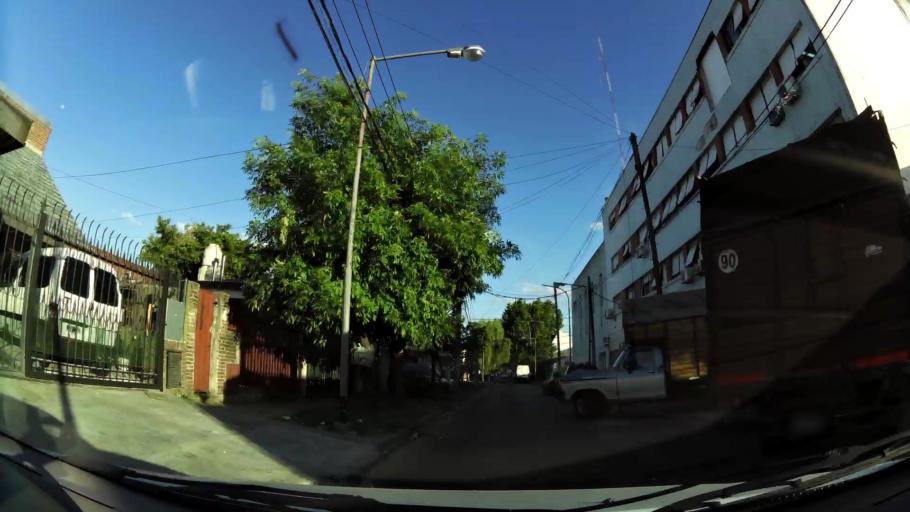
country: AR
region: Buenos Aires
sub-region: Partido de General San Martin
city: General San Martin
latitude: -34.5736
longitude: -58.5478
